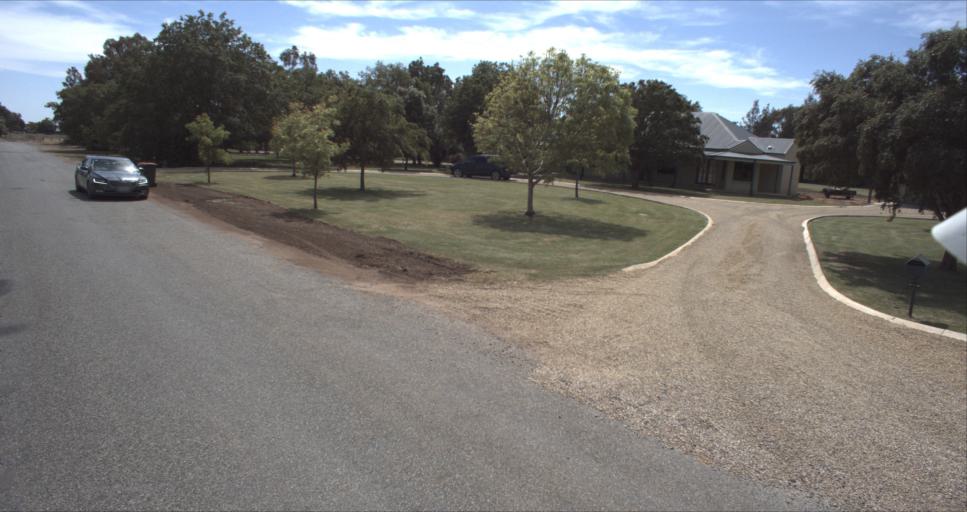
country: AU
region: New South Wales
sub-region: Leeton
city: Leeton
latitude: -34.5624
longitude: 146.4185
